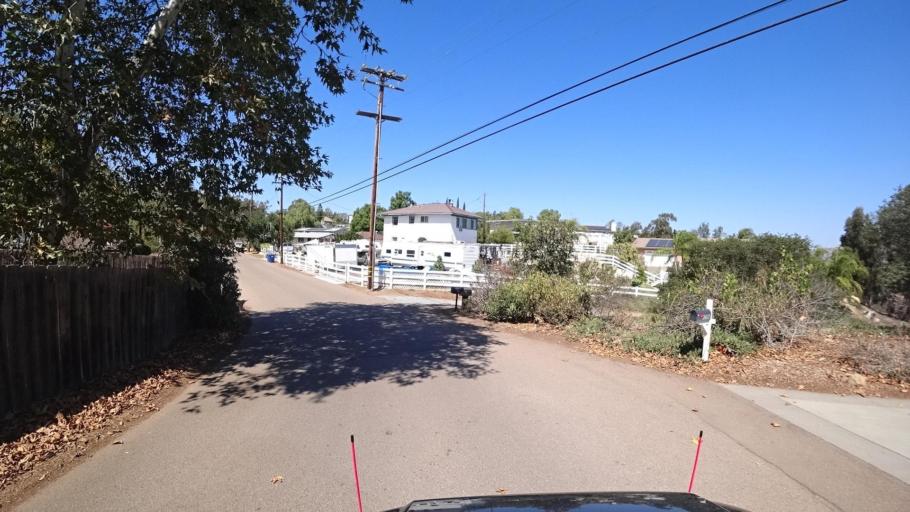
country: US
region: California
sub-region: San Diego County
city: Crest
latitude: 32.7996
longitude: -116.8637
